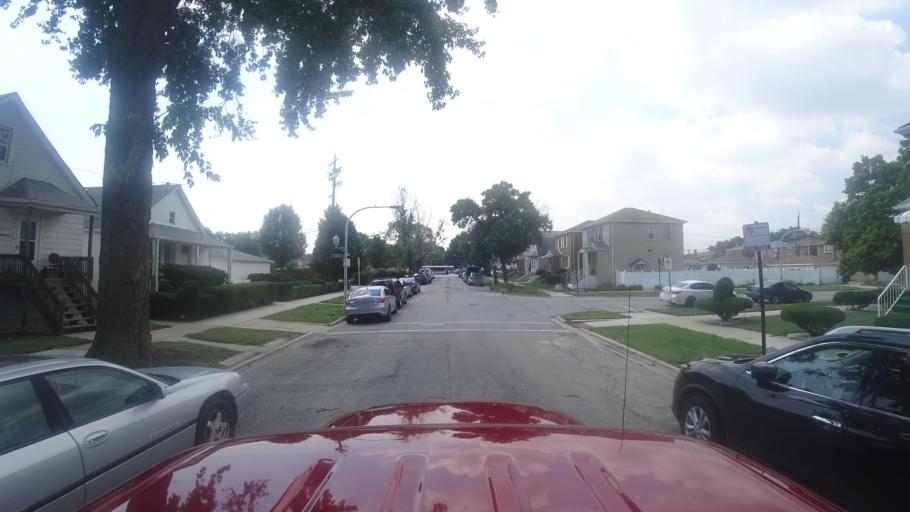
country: US
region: Illinois
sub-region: Cook County
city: Cicero
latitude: 41.8063
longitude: -87.7186
